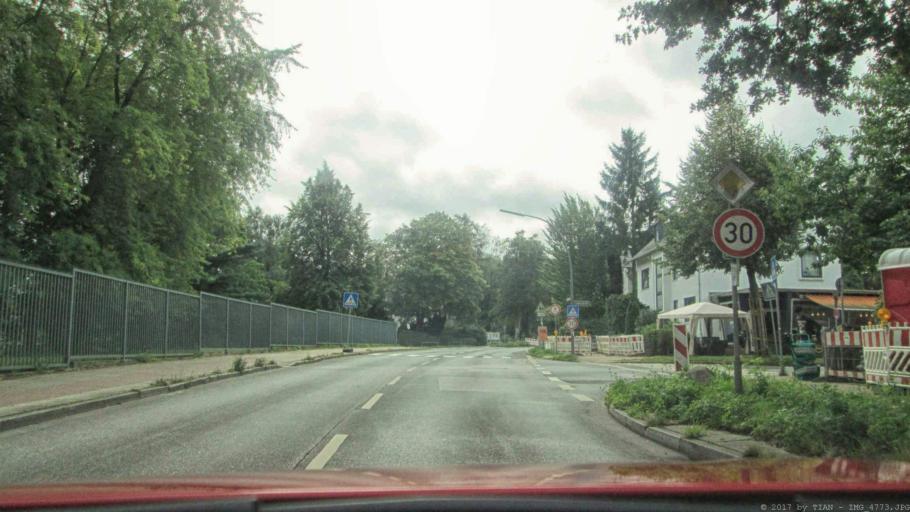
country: DE
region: Schleswig-Holstein
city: Halstenbek
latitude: 53.5641
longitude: 9.8262
